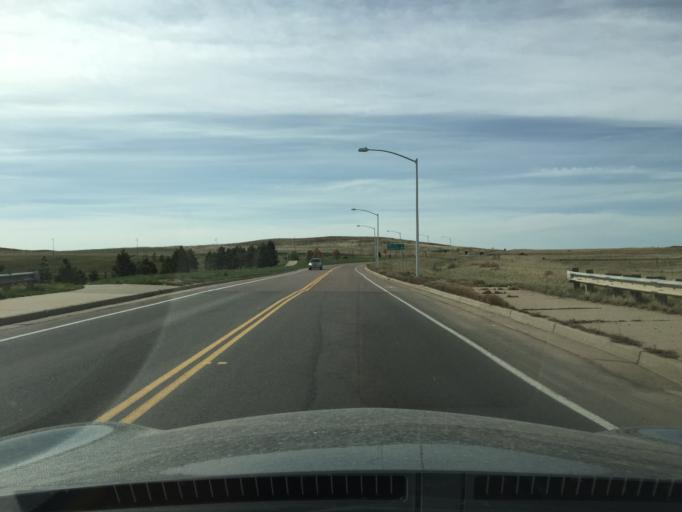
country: US
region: Colorado
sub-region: Boulder County
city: Lafayette
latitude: 39.9812
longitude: -105.0353
